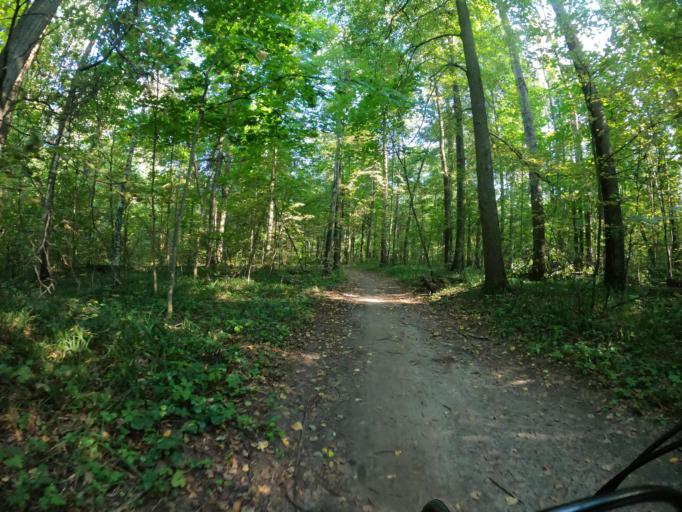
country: RU
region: Moskovskaya
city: Stupino
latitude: 54.8777
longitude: 38.0919
